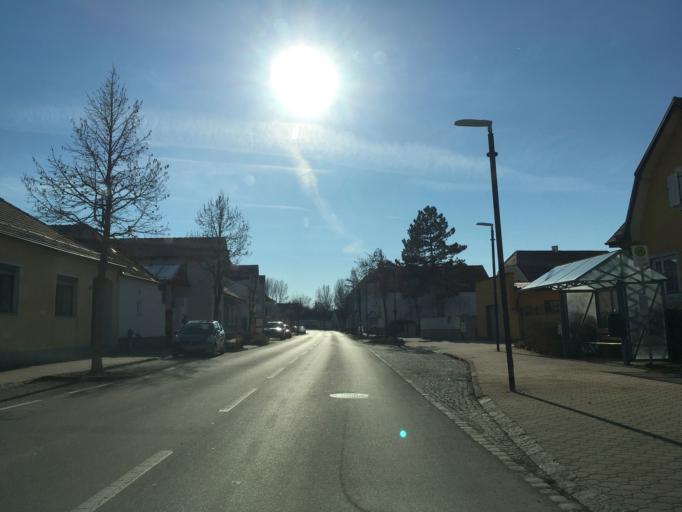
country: AT
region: Burgenland
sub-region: Eisenstadt-Umgebung
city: Wimpassing an der Leitha
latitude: 47.9181
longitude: 16.4296
